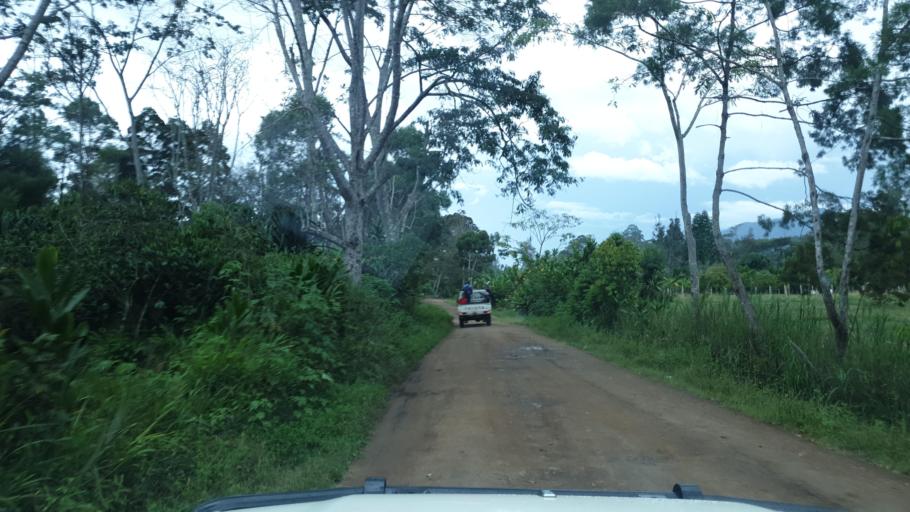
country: PG
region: Eastern Highlands
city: Goroka
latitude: -5.9742
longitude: 145.2770
